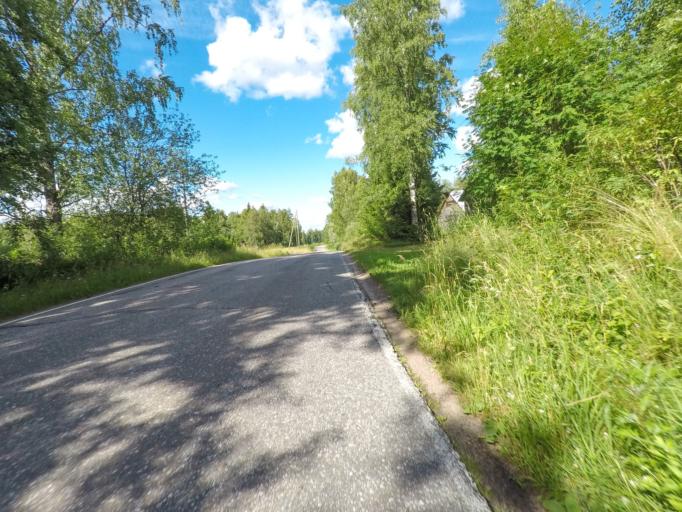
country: FI
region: South Karelia
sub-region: Lappeenranta
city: Joutseno
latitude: 61.1135
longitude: 28.3718
